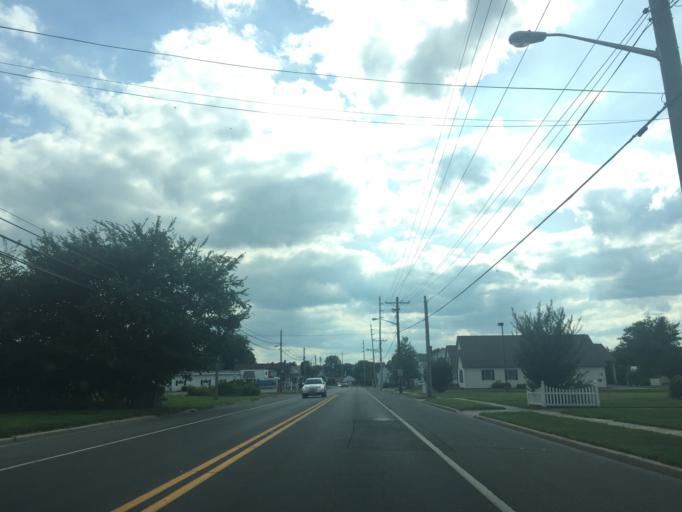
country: US
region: Delaware
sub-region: Sussex County
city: Georgetown
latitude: 38.6971
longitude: -75.3746
